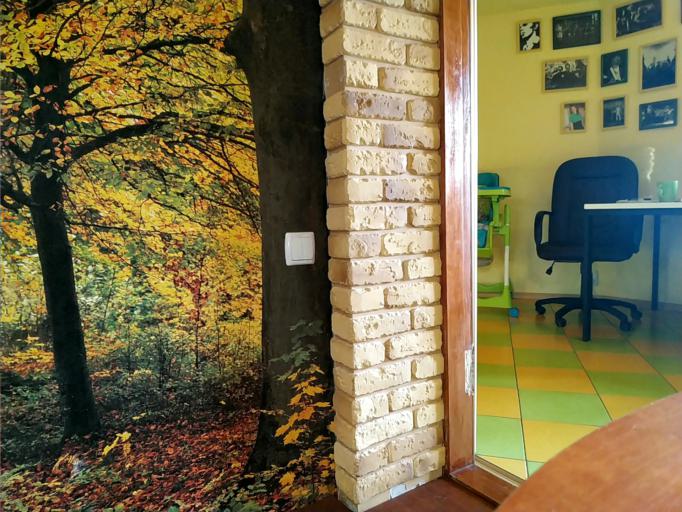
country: RU
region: Jaroslavl
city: Krasnyy Profintern
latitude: 57.9411
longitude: 40.5412
